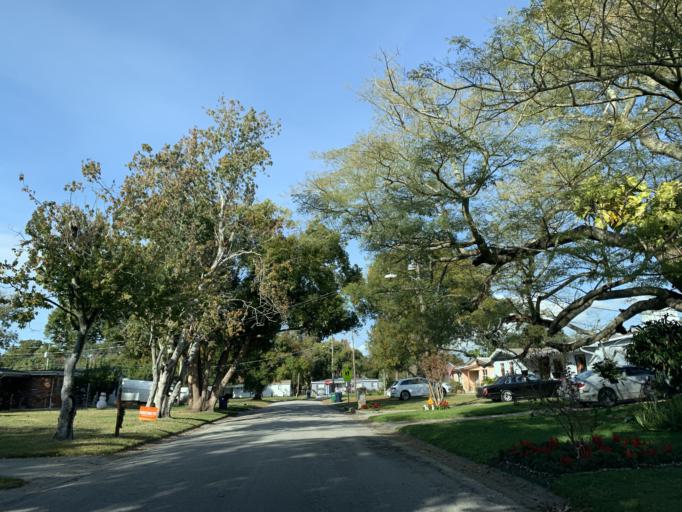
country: US
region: Florida
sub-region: Hillsborough County
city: Tampa
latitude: 27.8997
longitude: -82.5107
